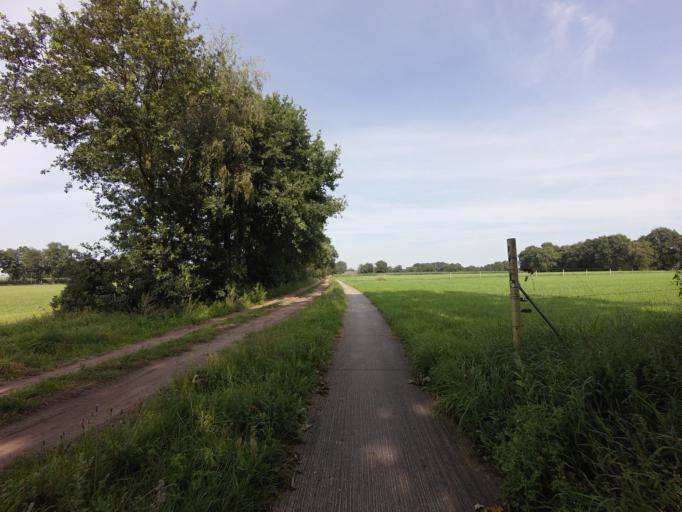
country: NL
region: Overijssel
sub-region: Gemeente Tubbergen
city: Tubbergen
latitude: 52.4420
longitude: 6.7971
